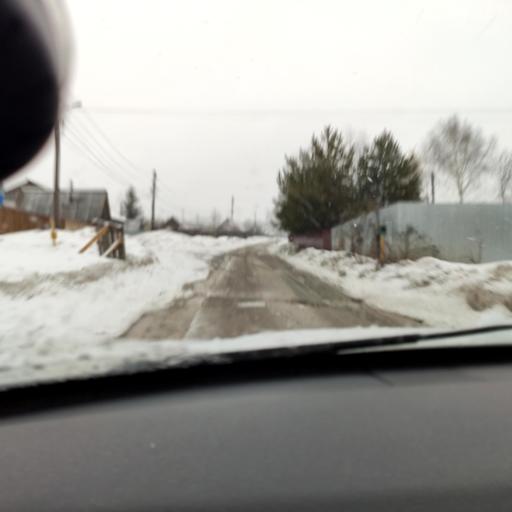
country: RU
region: Perm
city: Polazna
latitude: 58.1792
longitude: 56.4029
